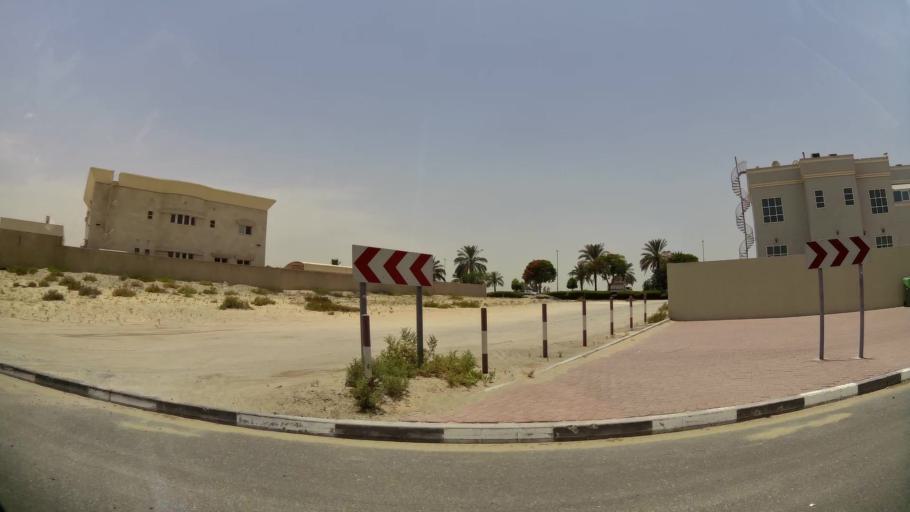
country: AE
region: Ash Shariqah
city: Sharjah
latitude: 25.2080
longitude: 55.3778
